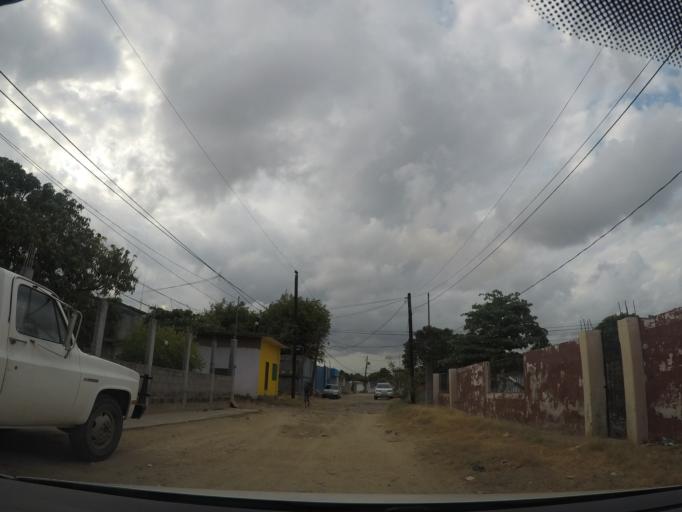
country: MX
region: Oaxaca
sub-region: Salina Cruz
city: Salina Cruz
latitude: 16.2131
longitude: -95.1997
